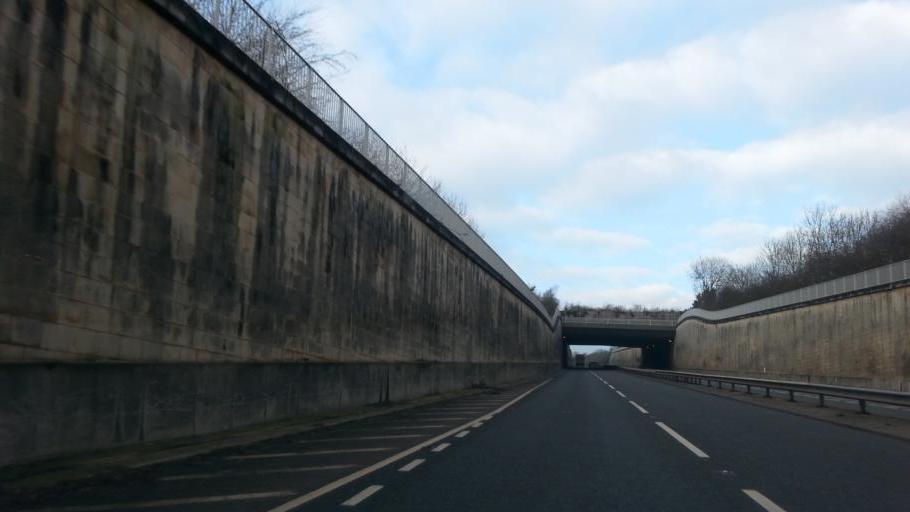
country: GB
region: England
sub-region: Bath and North East Somerset
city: Bath
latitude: 51.4013
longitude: -2.3383
